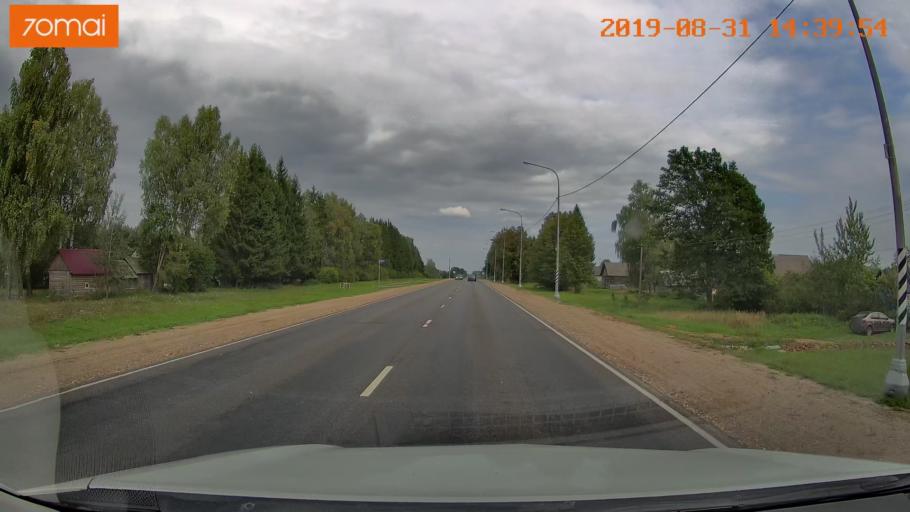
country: RU
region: Smolensk
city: Yekimovichi
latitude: 54.1944
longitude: 33.5622
